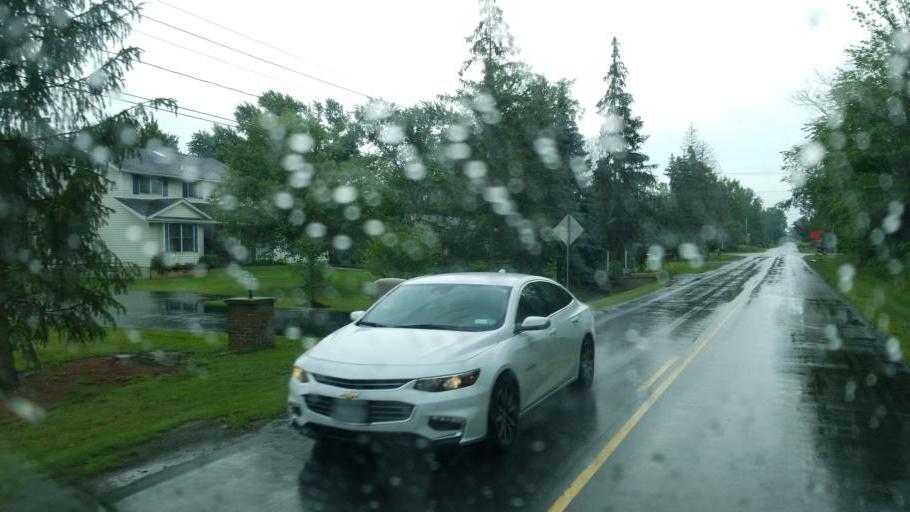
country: US
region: New York
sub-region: Niagara County
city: Ransomville
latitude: 43.2432
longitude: -78.8924
